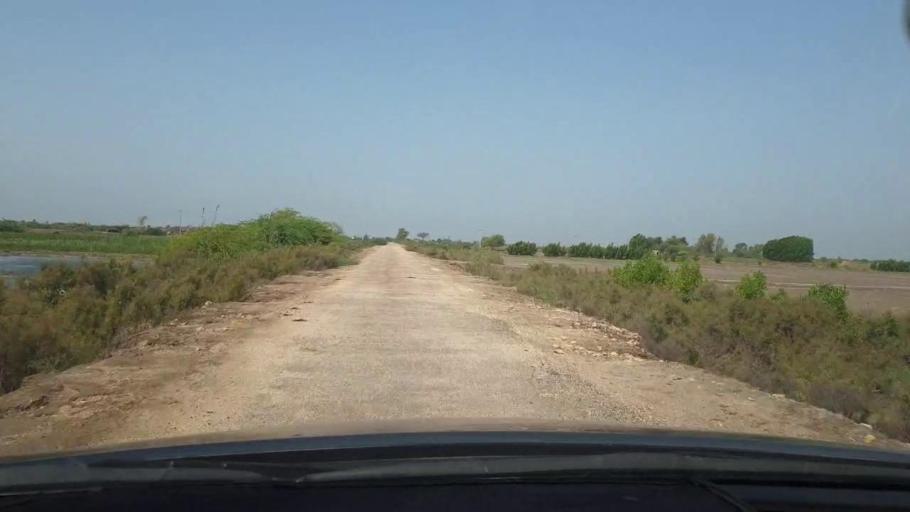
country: PK
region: Sindh
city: Tando Bago
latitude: 24.7092
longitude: 69.1179
